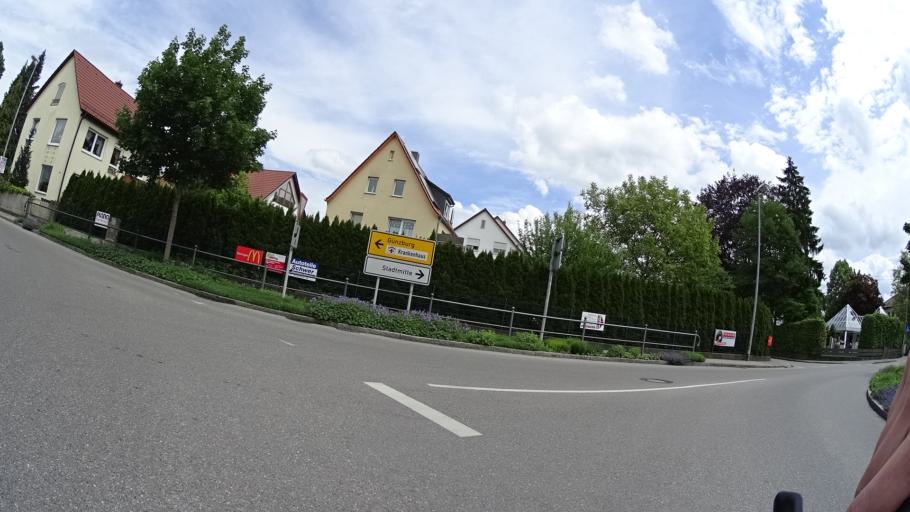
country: DE
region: Bavaria
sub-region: Swabia
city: Weissenhorn
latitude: 48.3094
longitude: 10.1593
